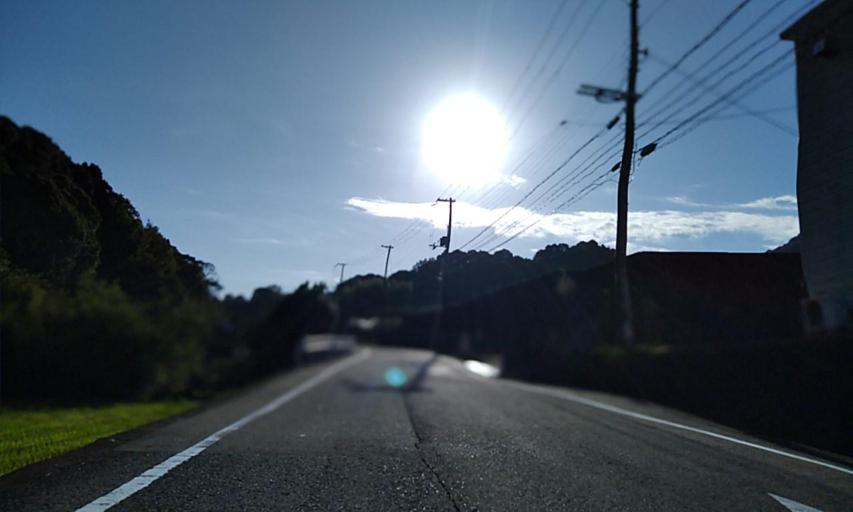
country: JP
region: Wakayama
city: Iwade
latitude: 34.1564
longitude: 135.2965
